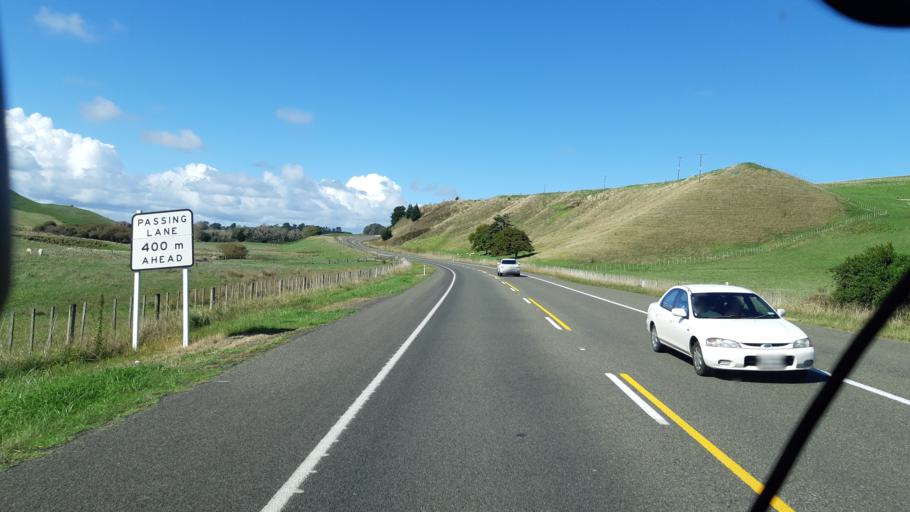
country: NZ
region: Manawatu-Wanganui
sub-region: Wanganui District
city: Wanganui
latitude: -39.9675
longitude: 175.1028
